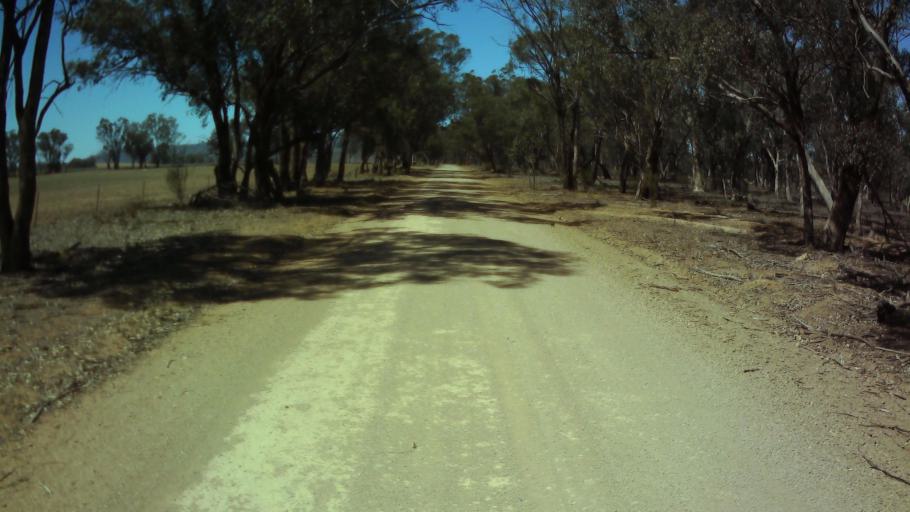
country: AU
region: New South Wales
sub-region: Weddin
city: Grenfell
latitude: -33.9033
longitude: 148.0819
